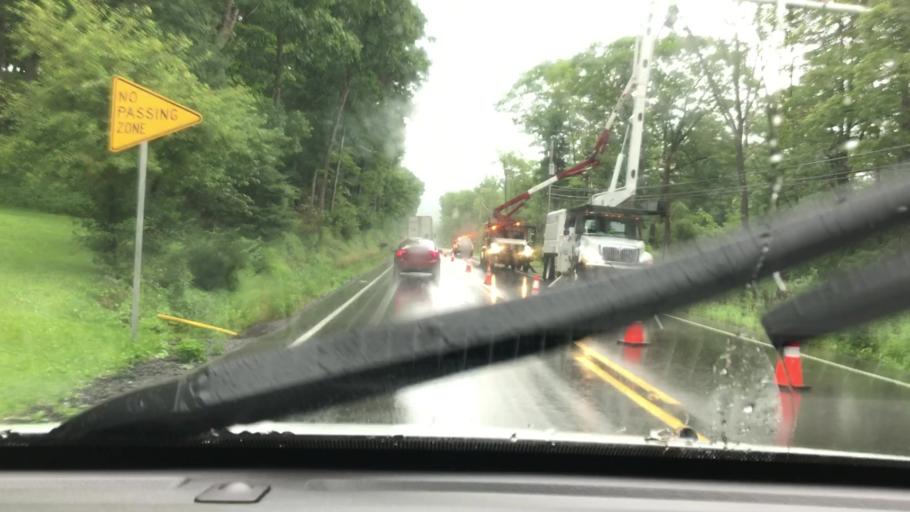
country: US
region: Pennsylvania
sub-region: Blair County
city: Tyrone
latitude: 40.7381
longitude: -78.1958
